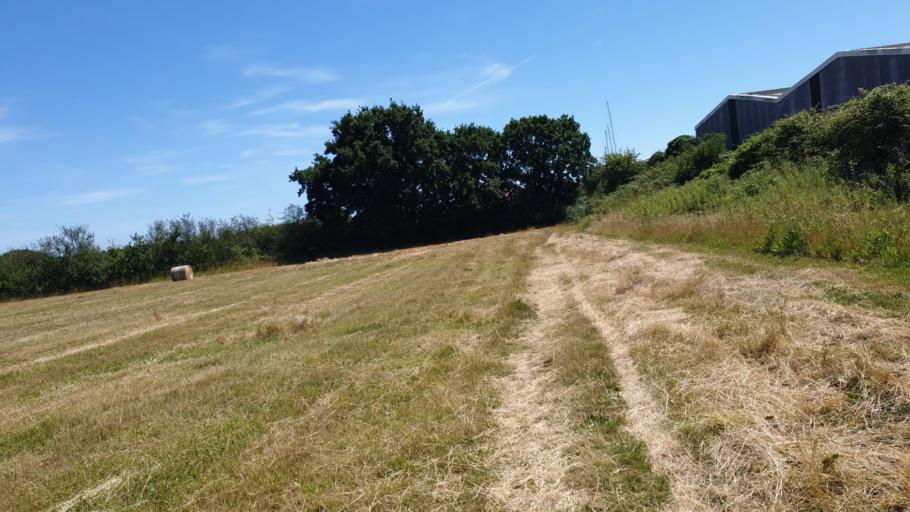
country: GB
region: England
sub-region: Essex
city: Brightlingsea
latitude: 51.8071
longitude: 1.0276
